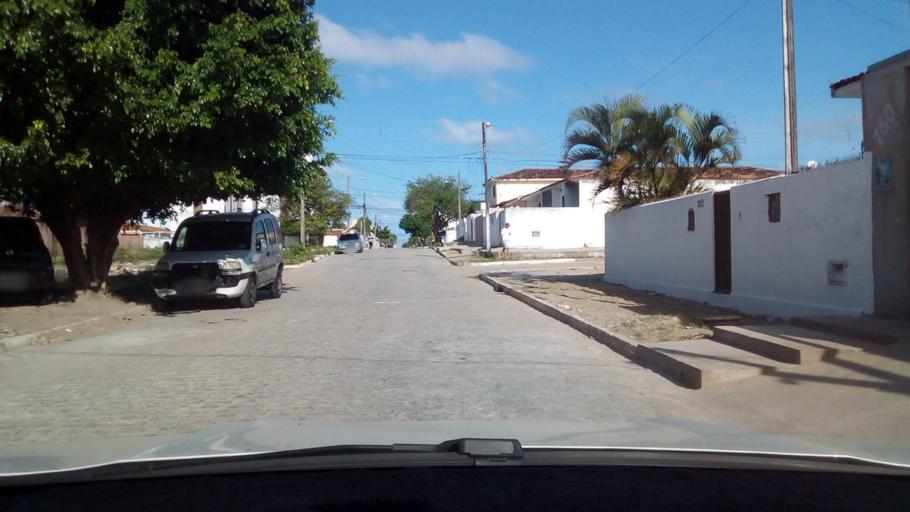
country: BR
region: Paraiba
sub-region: Joao Pessoa
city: Joao Pessoa
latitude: -7.1546
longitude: -34.8316
